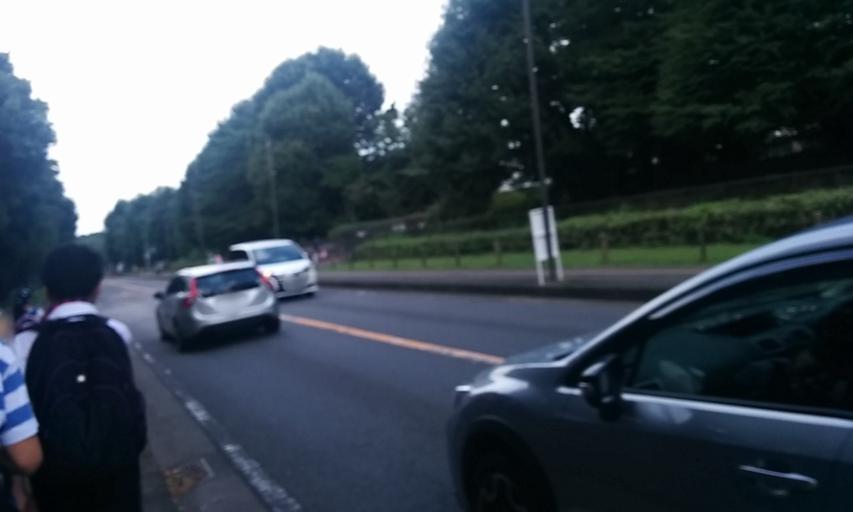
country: JP
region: Tokyo
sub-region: Machida-shi
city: Machida
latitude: 35.5598
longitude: 139.3952
